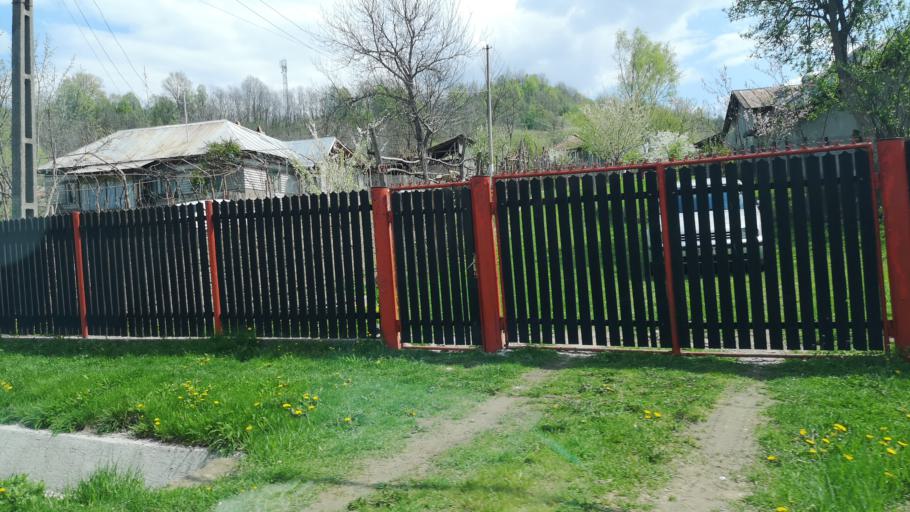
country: RO
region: Prahova
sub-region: Comuna Soimari
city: Soimari
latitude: 45.1734
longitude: 26.2114
